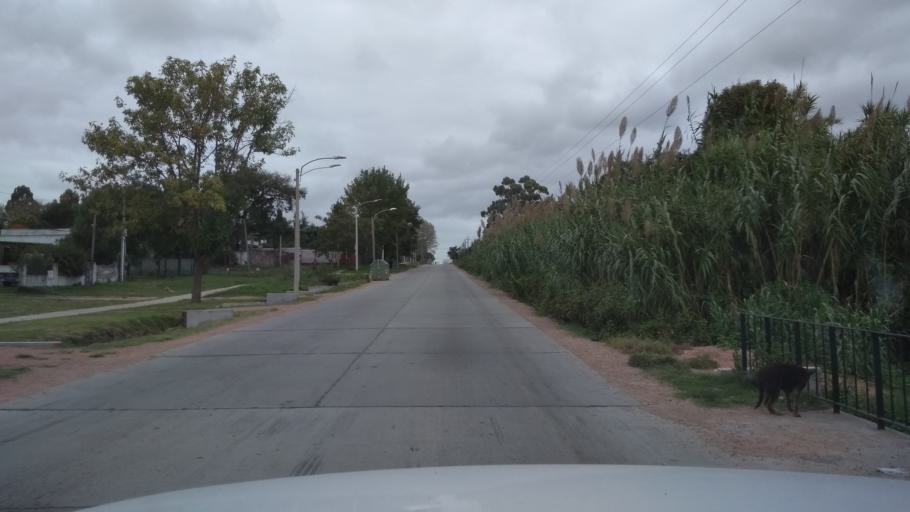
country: UY
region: Canelones
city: Toledo
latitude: -34.7850
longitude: -56.1403
